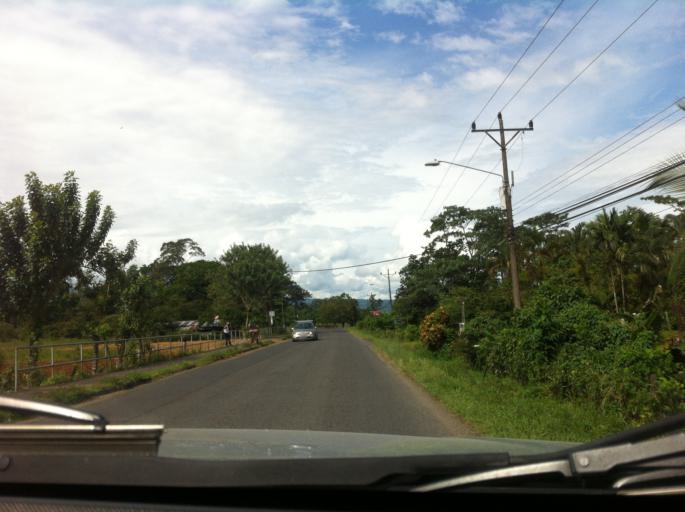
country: CR
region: Limon
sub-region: Canton de Pococi
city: Guapiles
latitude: 10.3203
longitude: -83.9181
